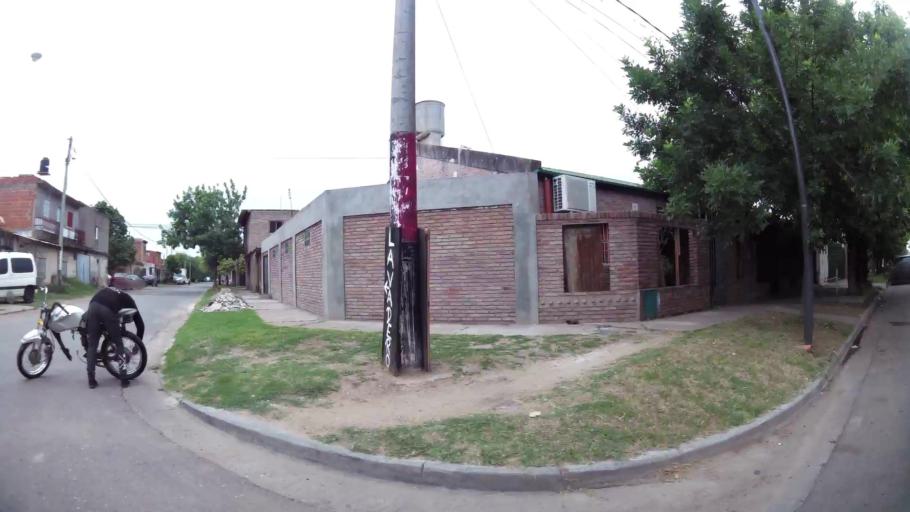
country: AR
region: Santa Fe
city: Gobernador Galvez
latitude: -33.0114
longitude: -60.6615
